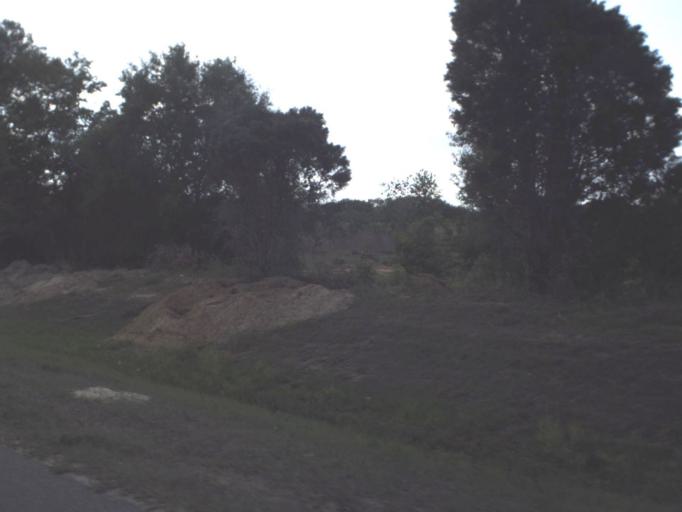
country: US
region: Florida
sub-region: Lake County
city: Mount Dora
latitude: 28.8007
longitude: -81.5947
